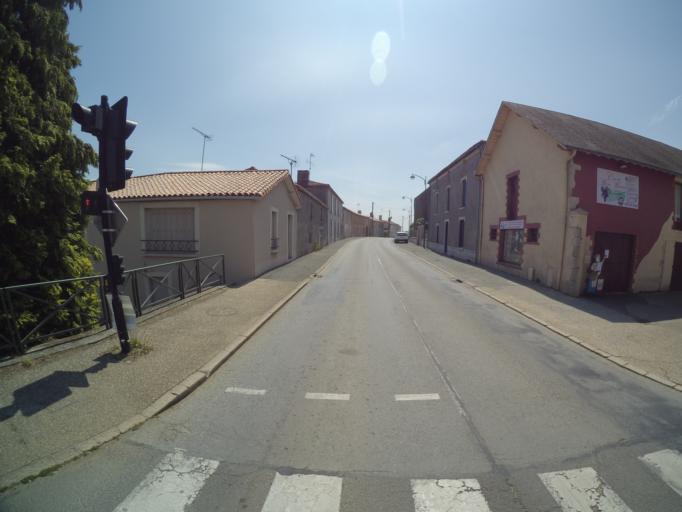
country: FR
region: Pays de la Loire
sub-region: Departement de la Vendee
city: Saint-Michel-Mont-Mercure
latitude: 46.8294
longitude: -0.8833
